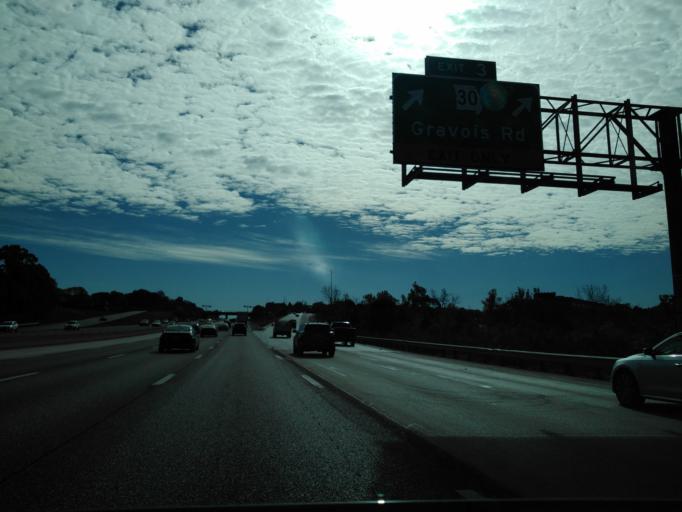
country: US
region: Missouri
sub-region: Saint Louis County
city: Sunset Hills
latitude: 38.5290
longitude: -90.4039
